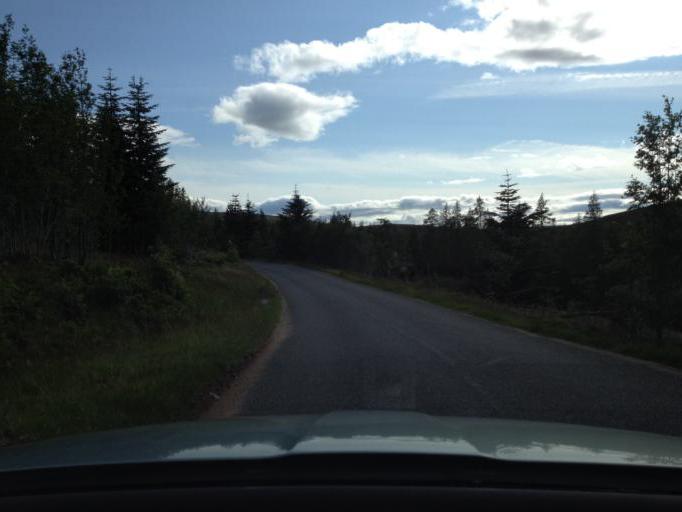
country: GB
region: Scotland
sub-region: Aberdeenshire
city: Banchory
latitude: 56.9534
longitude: -2.5849
